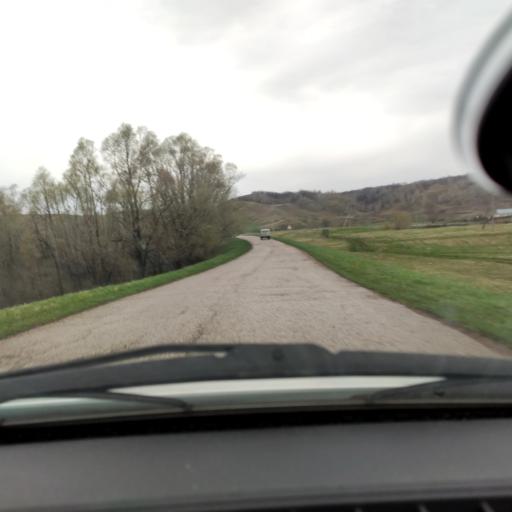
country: RU
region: Bashkortostan
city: Tolbazy
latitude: 54.1706
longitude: 55.9467
